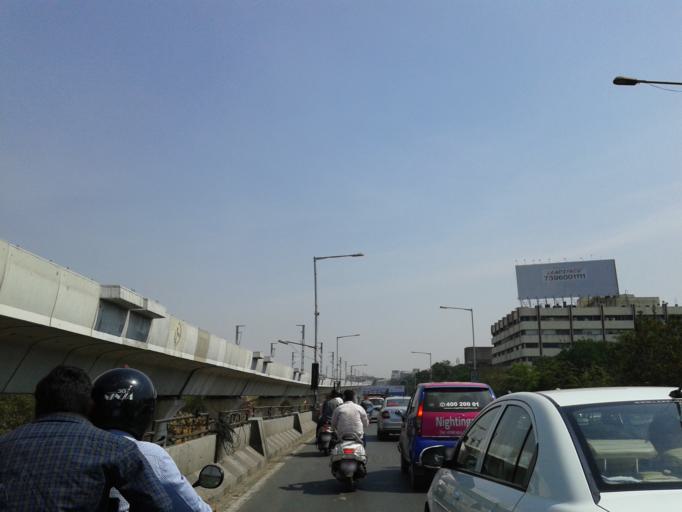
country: IN
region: Telangana
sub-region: Hyderabad
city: Malkajgiri
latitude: 17.4434
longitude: 78.4875
